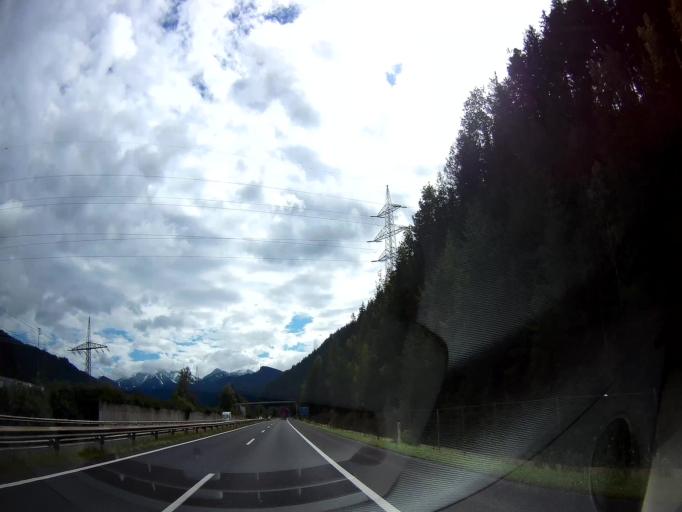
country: AT
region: Styria
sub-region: Politischer Bezirk Leoben
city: Traboch
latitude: 47.3623
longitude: 14.9982
